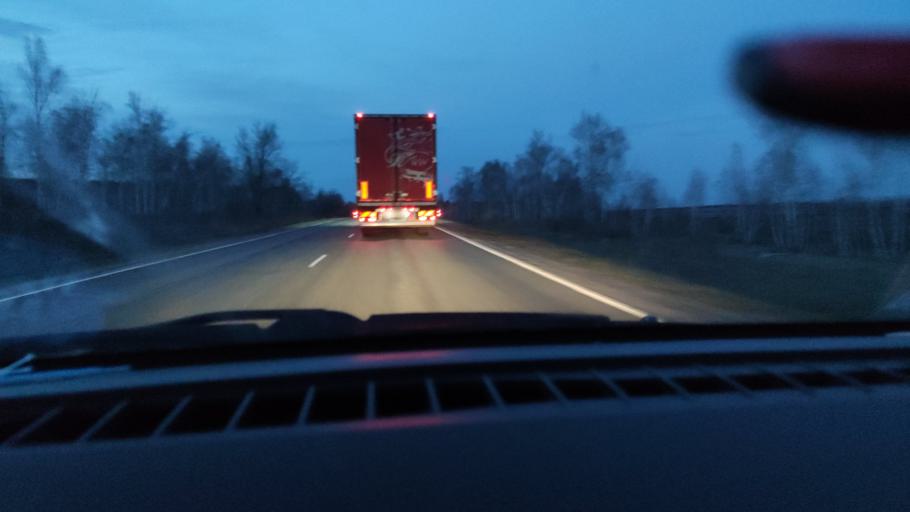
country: RU
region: Saratov
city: Sennoy
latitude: 52.1131
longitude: 46.8333
